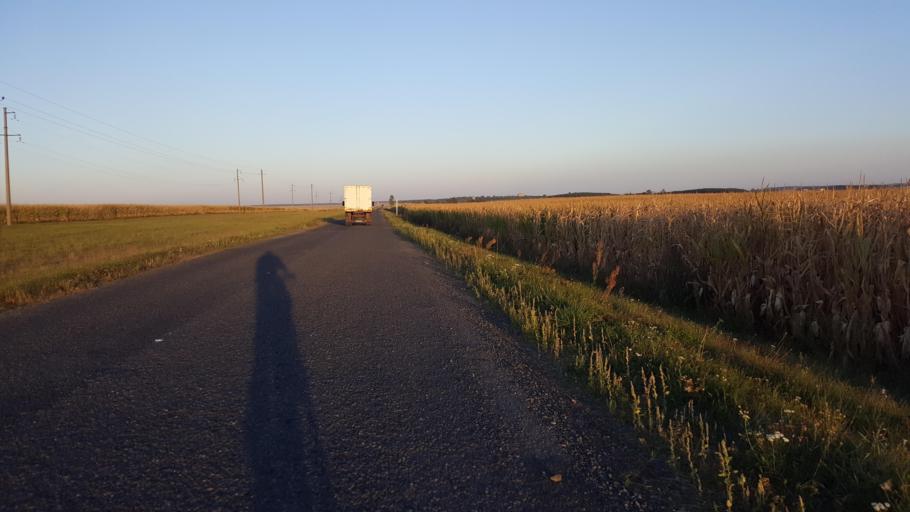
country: BY
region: Brest
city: Charnawchytsy
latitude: 52.2915
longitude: 23.5612
